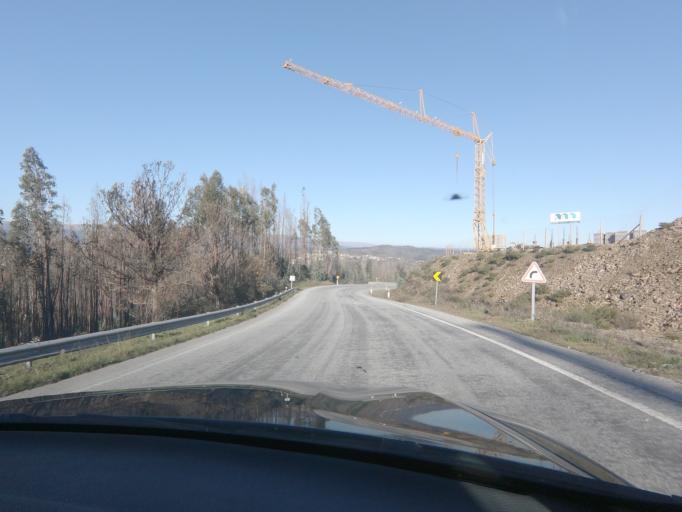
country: PT
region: Viseu
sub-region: Vouzela
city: Vouzela
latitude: 40.7239
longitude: -8.1320
